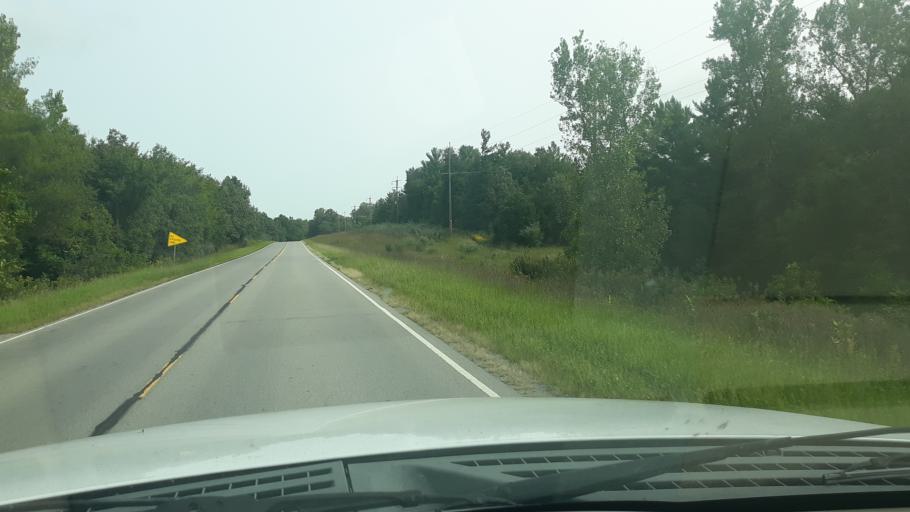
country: US
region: Illinois
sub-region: White County
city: Norris City
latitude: 37.9162
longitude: -88.3538
